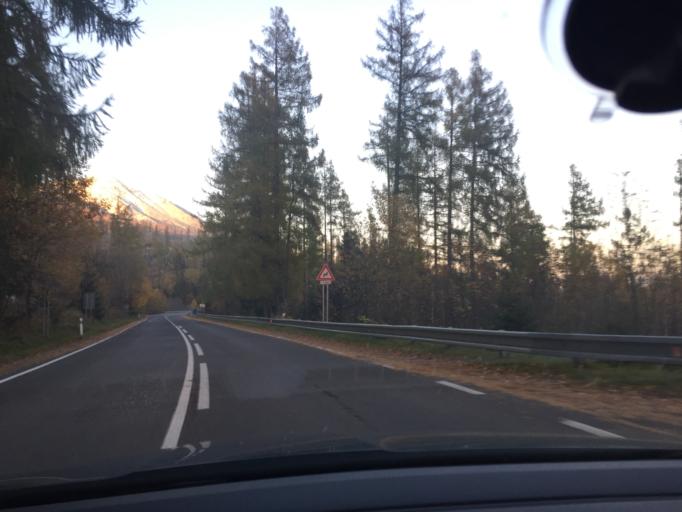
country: SK
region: Presovsky
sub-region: Okres Poprad
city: Strba
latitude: 49.1173
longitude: 20.1260
